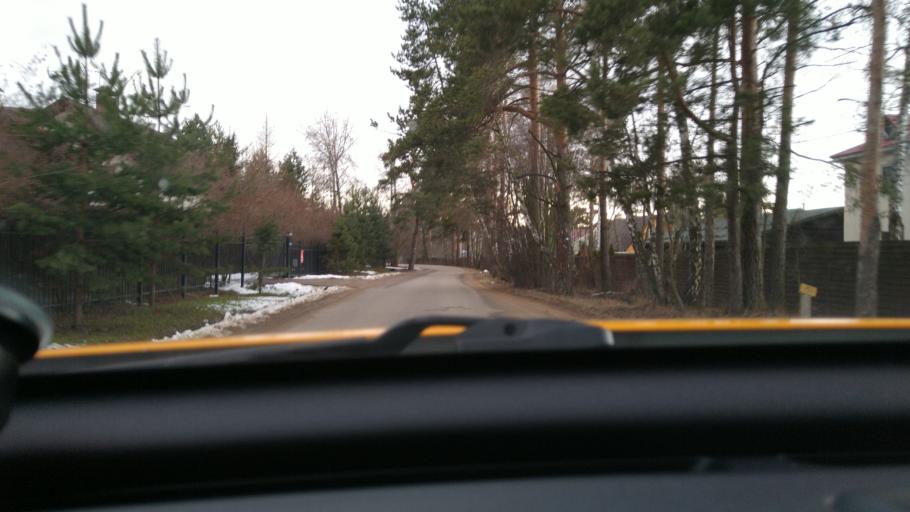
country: RU
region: Moskovskaya
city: Petrovo-Dal'neye
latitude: 55.7656
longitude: 37.2063
